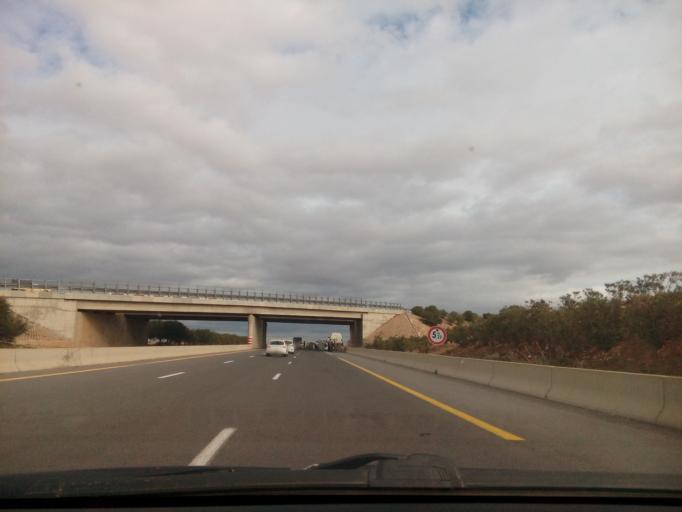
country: DZ
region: Sidi Bel Abbes
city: Sidi Bel Abbes
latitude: 35.1779
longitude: -0.7476
